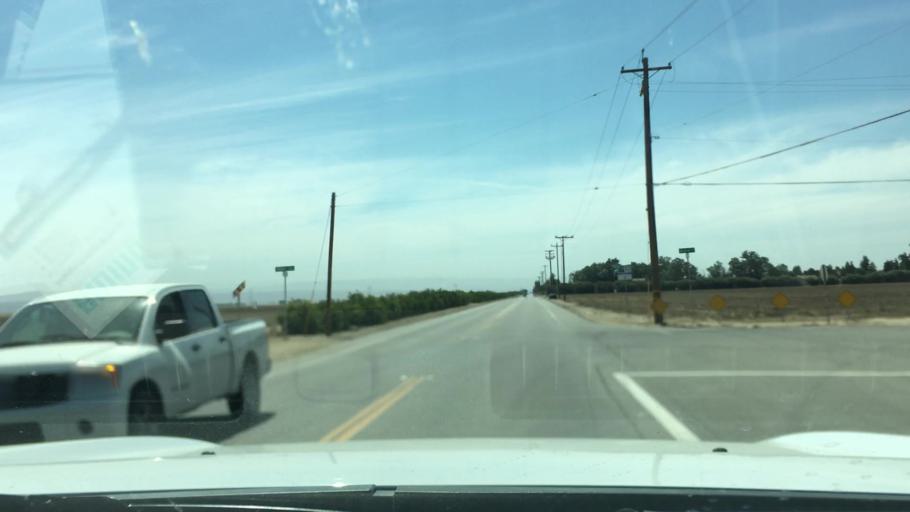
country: US
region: California
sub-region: Kern County
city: Rosedale
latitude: 35.3544
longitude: -119.1986
